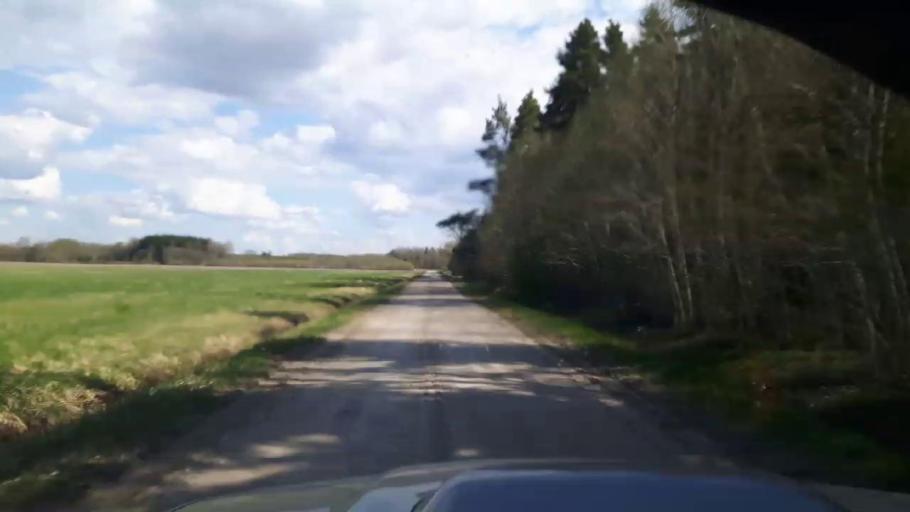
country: EE
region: Paernumaa
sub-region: Tootsi vald
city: Tootsi
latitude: 58.4489
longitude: 24.8346
